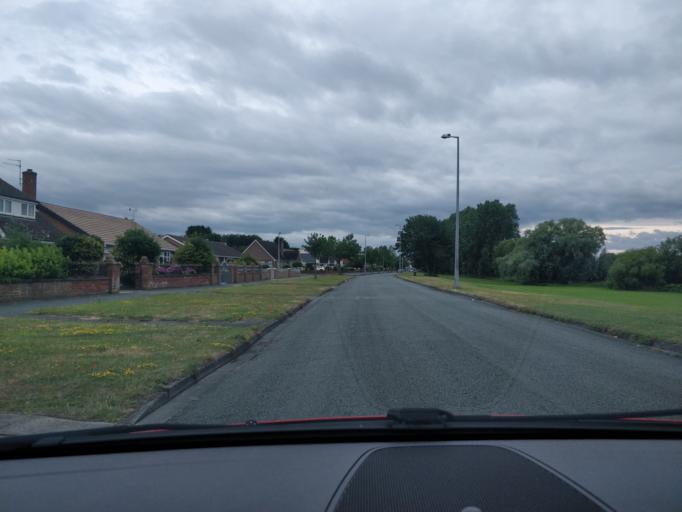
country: GB
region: England
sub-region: Sefton
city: Southport
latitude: 53.6602
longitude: -2.9883
